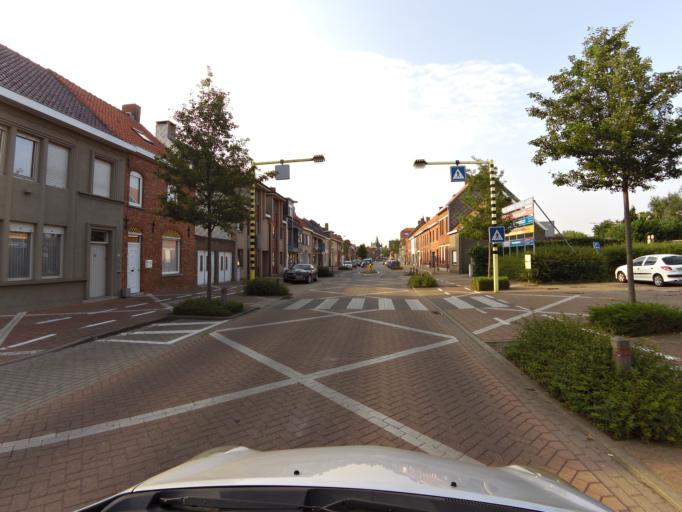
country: BE
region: Flanders
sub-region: Provincie West-Vlaanderen
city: Torhout
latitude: 51.0591
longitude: 3.1029
